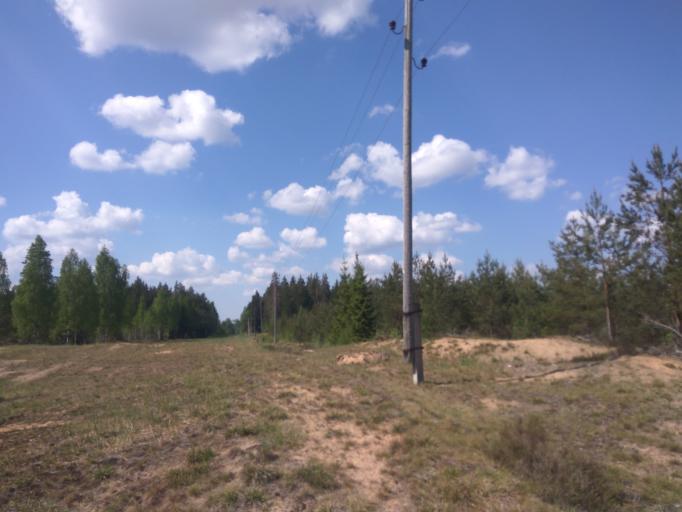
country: LV
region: Kuldigas Rajons
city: Kuldiga
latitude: 57.1849
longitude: 21.9940
